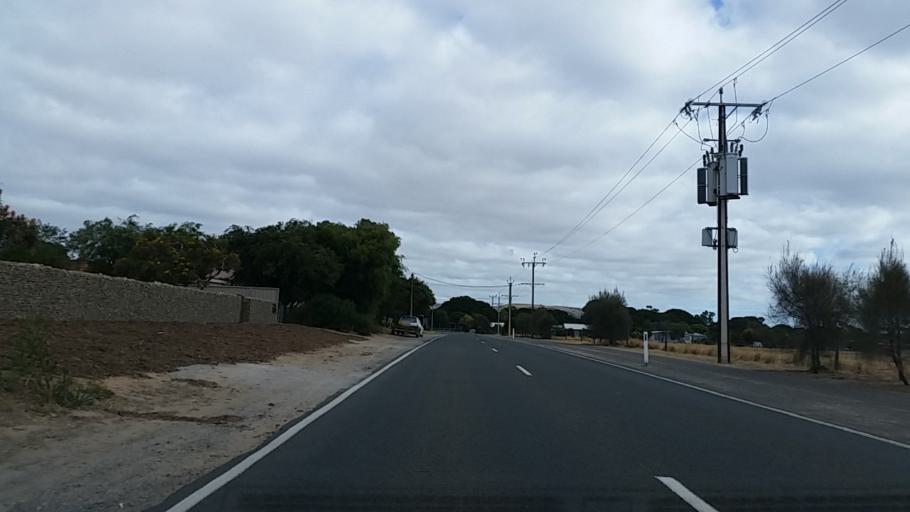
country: AU
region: South Australia
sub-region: Yankalilla
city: Normanville
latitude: -35.4424
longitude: 138.3171
